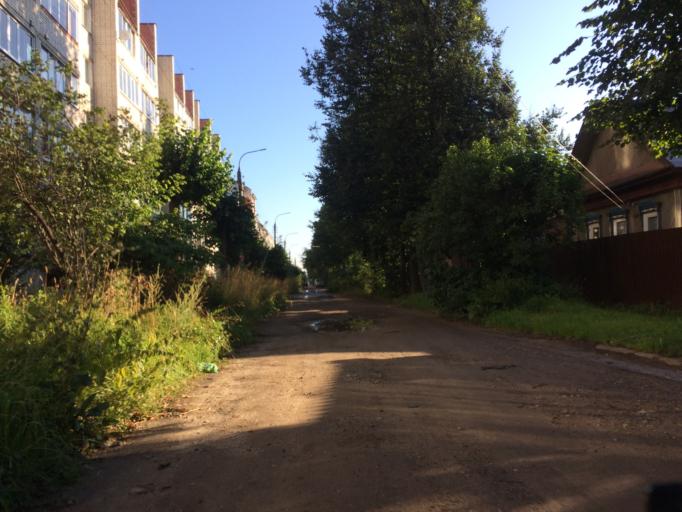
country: RU
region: Mariy-El
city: Yoshkar-Ola
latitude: 56.6480
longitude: 47.8888
